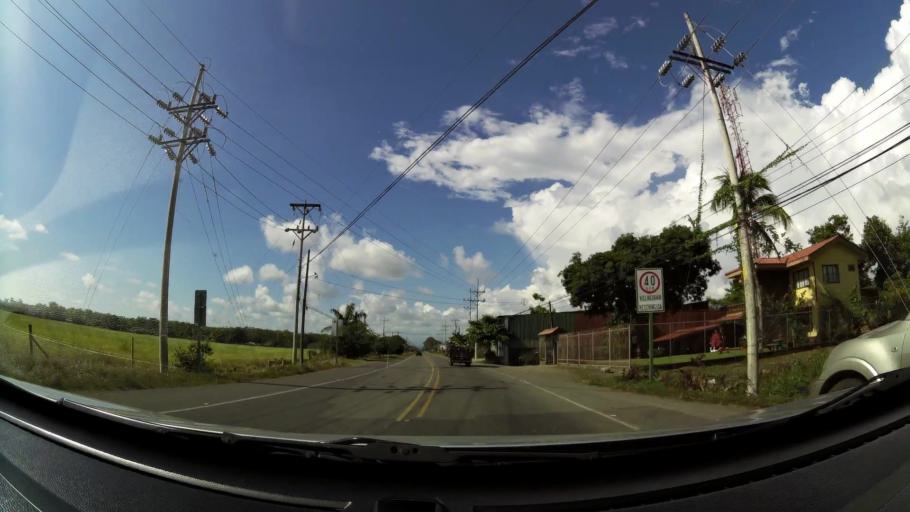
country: CR
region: Puntarenas
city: Quepos
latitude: 9.4575
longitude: -84.1784
